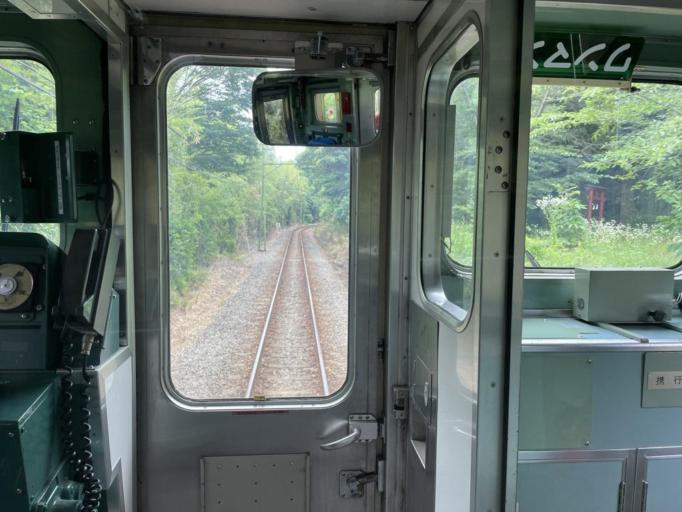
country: JP
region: Gunma
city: Takasaki
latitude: 36.2835
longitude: 139.0313
